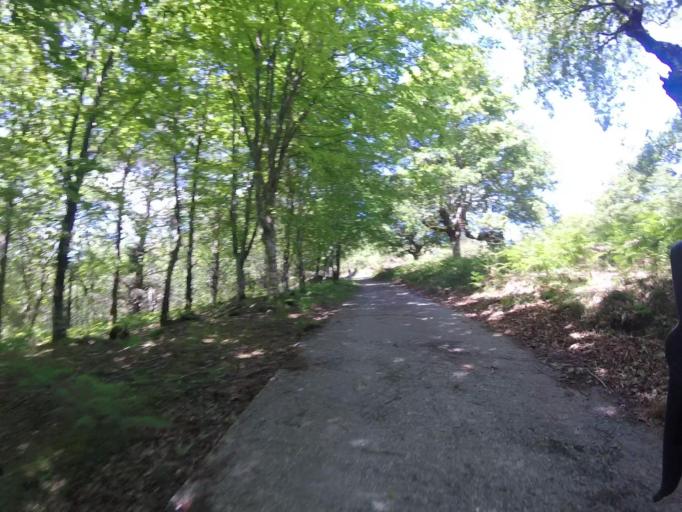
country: ES
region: Navarre
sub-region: Provincia de Navarra
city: Lesaka
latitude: 43.2430
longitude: -1.7358
